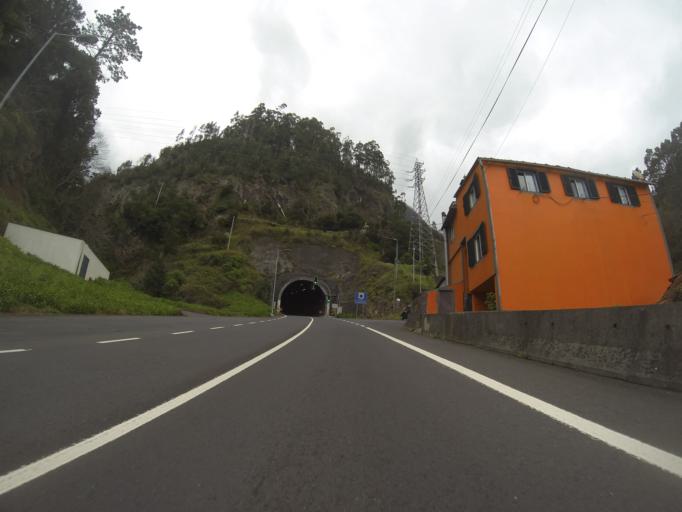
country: PT
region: Madeira
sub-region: Camara de Lobos
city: Curral das Freiras
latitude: 32.7413
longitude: -17.0176
